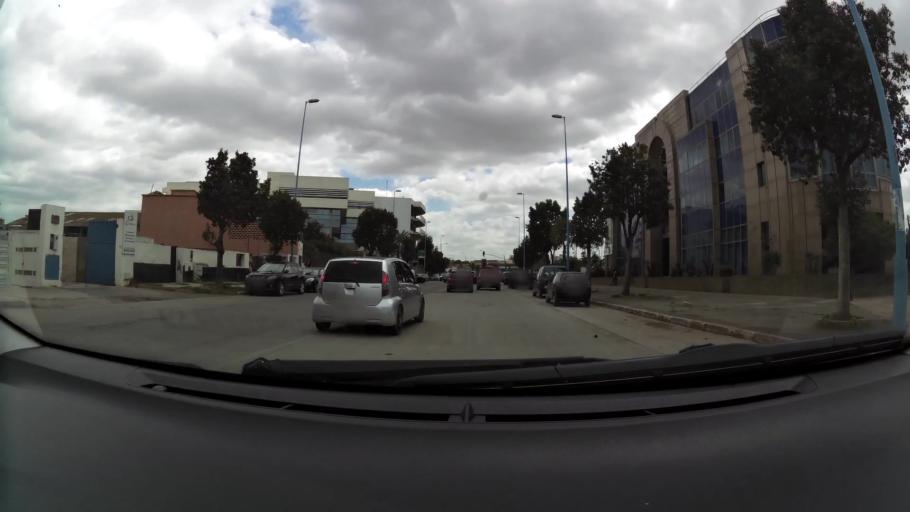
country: MA
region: Grand Casablanca
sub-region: Casablanca
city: Casablanca
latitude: 33.6046
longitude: -7.5467
